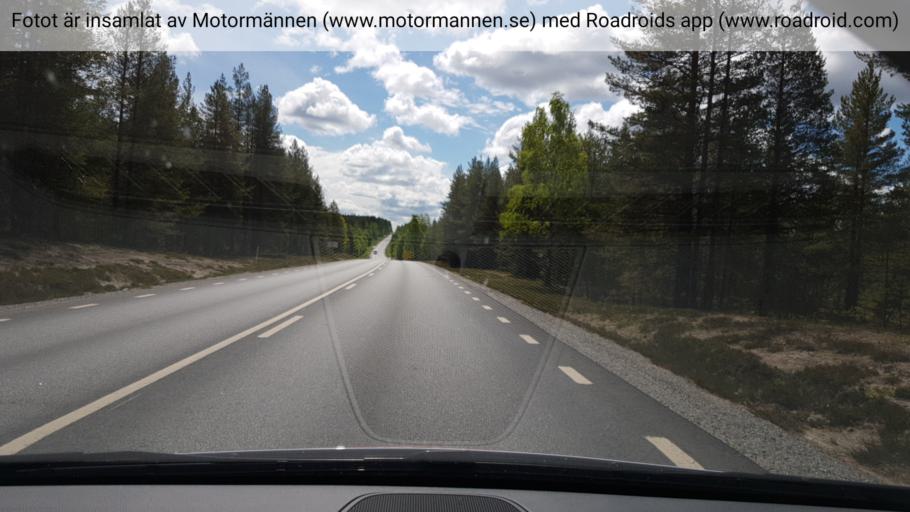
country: SE
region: Vaesterbotten
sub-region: Vannas Kommun
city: Vannasby
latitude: 64.0628
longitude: 19.9927
